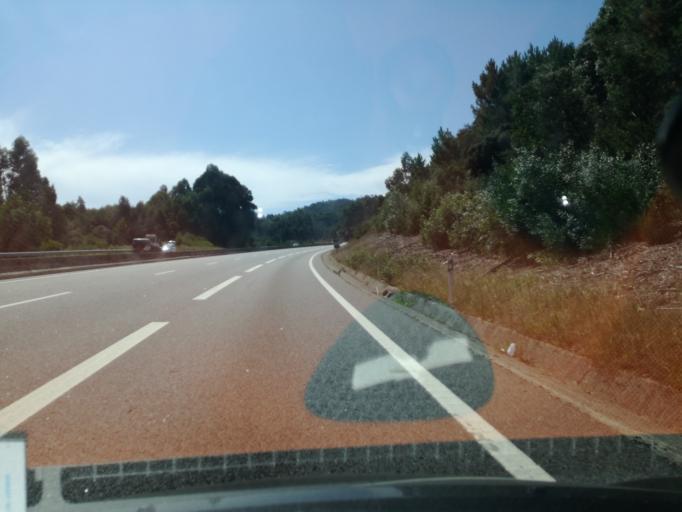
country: PT
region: Viana do Castelo
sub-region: Caminha
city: Vila Praia de Ancora
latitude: 41.7858
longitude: -8.7888
